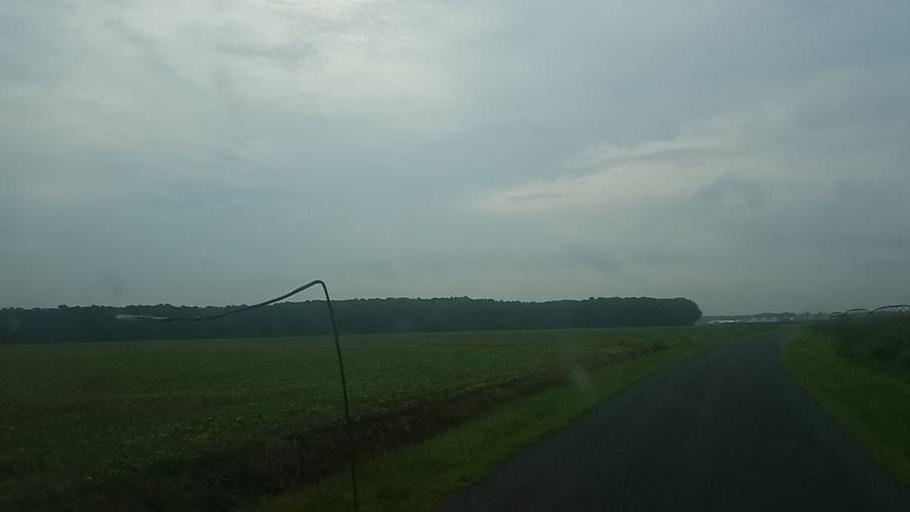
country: US
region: Delaware
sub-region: Sussex County
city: Selbyville
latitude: 38.4481
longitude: -75.2776
